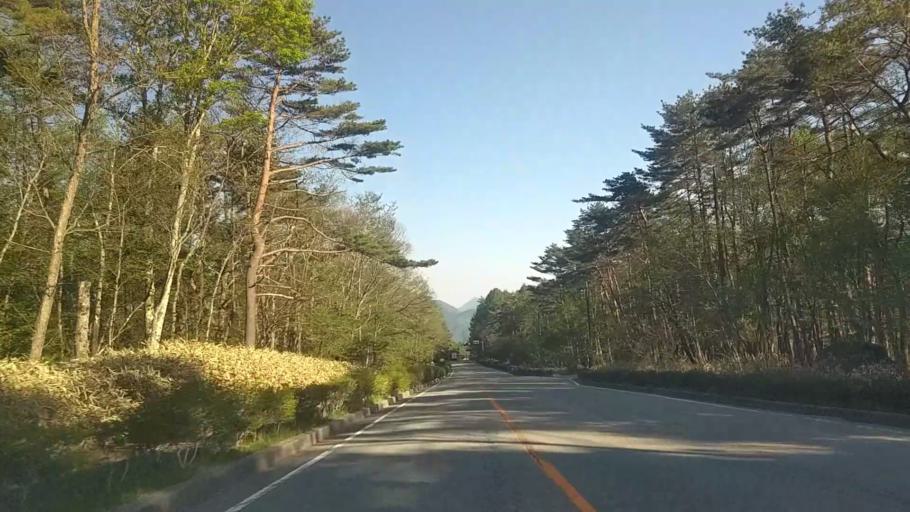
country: JP
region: Yamanashi
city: Nirasaki
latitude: 35.9277
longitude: 138.4302
